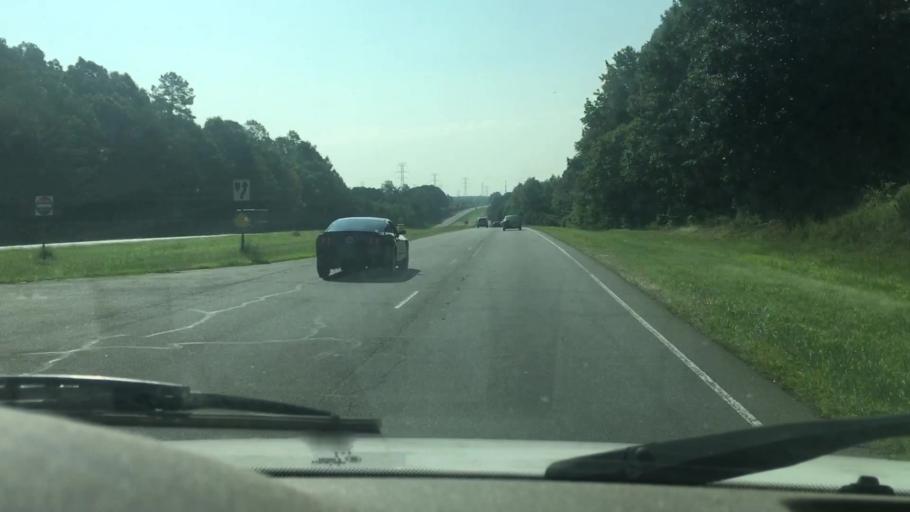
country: US
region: North Carolina
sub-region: Gaston County
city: Mount Holly
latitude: 35.3319
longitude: -80.9544
